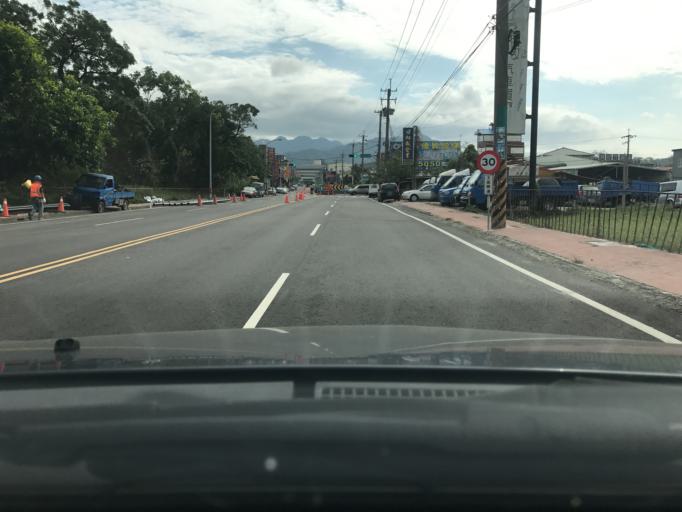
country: TW
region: Taiwan
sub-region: Hsinchu
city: Zhubei
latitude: 24.7285
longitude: 121.0995
